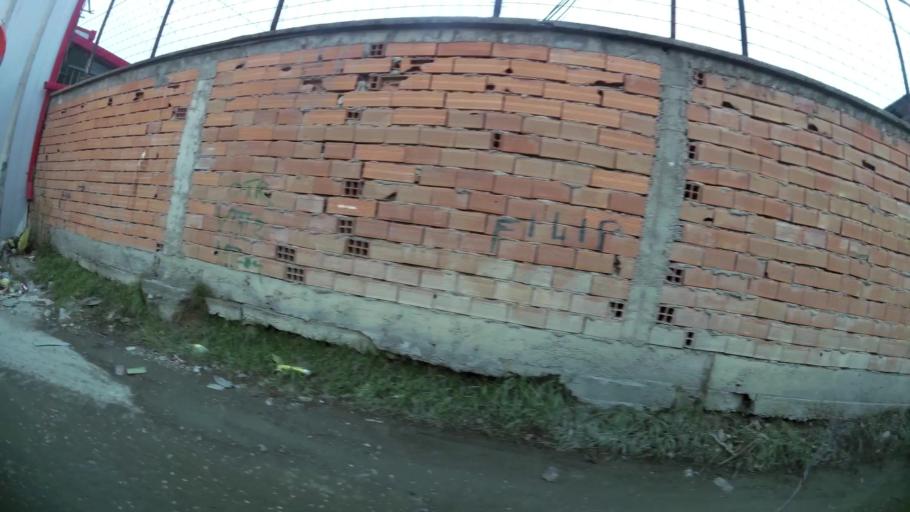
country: MK
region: Suto Orizari
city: Suto Orizare
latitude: 42.0300
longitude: 21.4306
